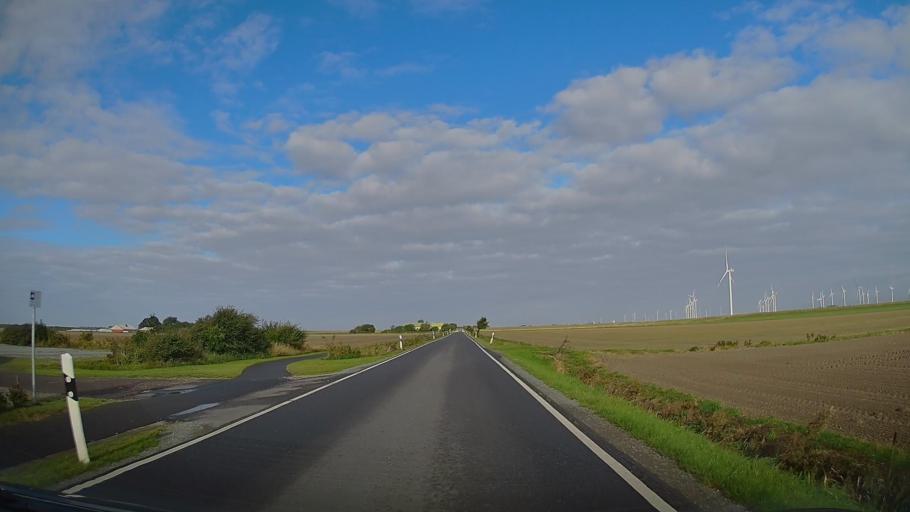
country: DE
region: Schleswig-Holstein
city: Reussenkoge
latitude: 54.5865
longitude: 8.9223
